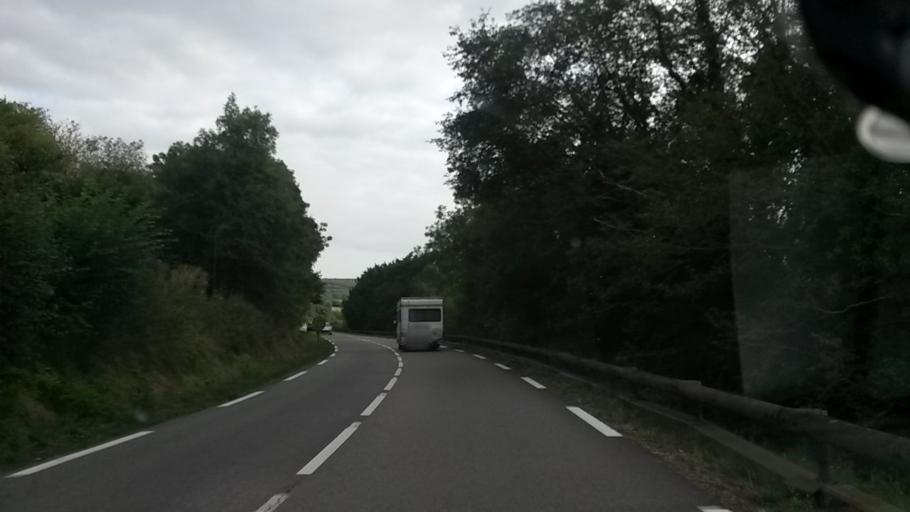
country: FR
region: Haute-Normandie
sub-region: Departement de l'Eure
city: Gravigny
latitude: 49.0652
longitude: 1.1742
